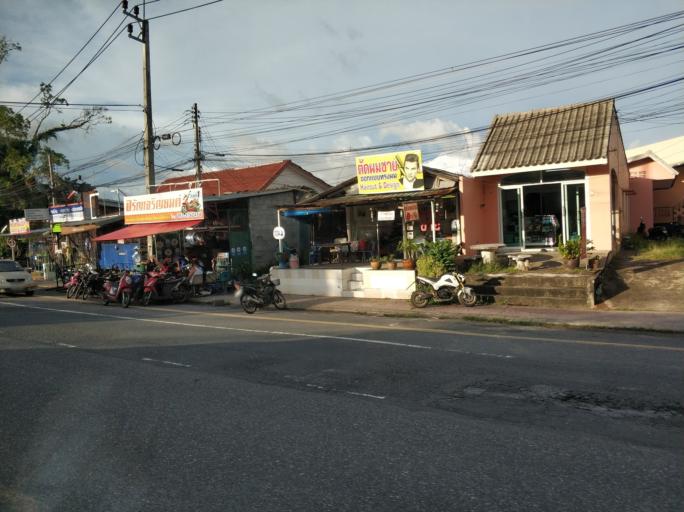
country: TH
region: Phuket
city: Kathu
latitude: 7.9028
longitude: 98.3362
